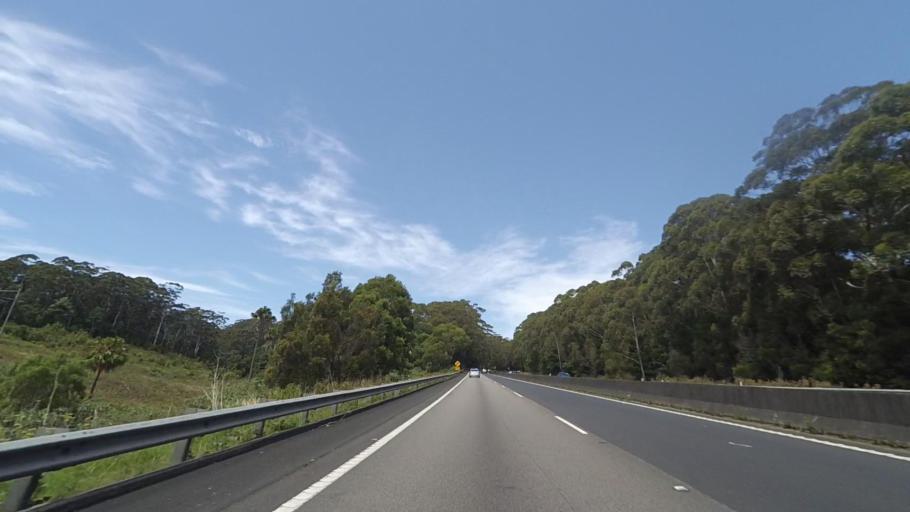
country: AU
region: New South Wales
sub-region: Wollongong
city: Bulli
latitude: -34.3418
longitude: 150.8774
